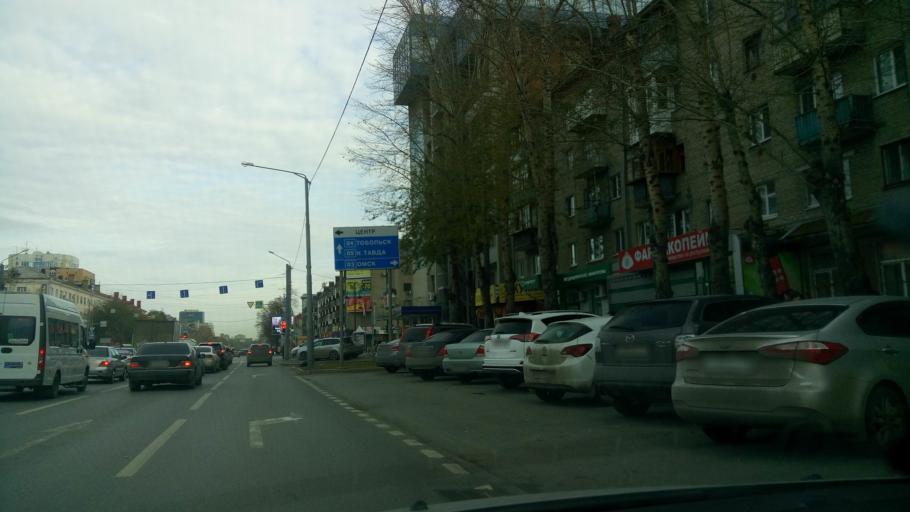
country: RU
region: Tjumen
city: Tyumen
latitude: 57.1373
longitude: 65.5682
